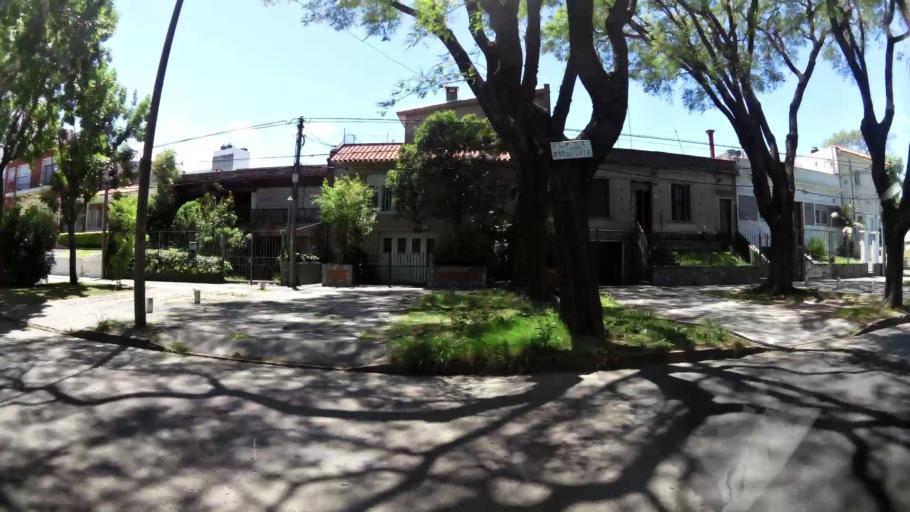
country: UY
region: Montevideo
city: Montevideo
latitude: -34.8963
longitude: -56.1426
